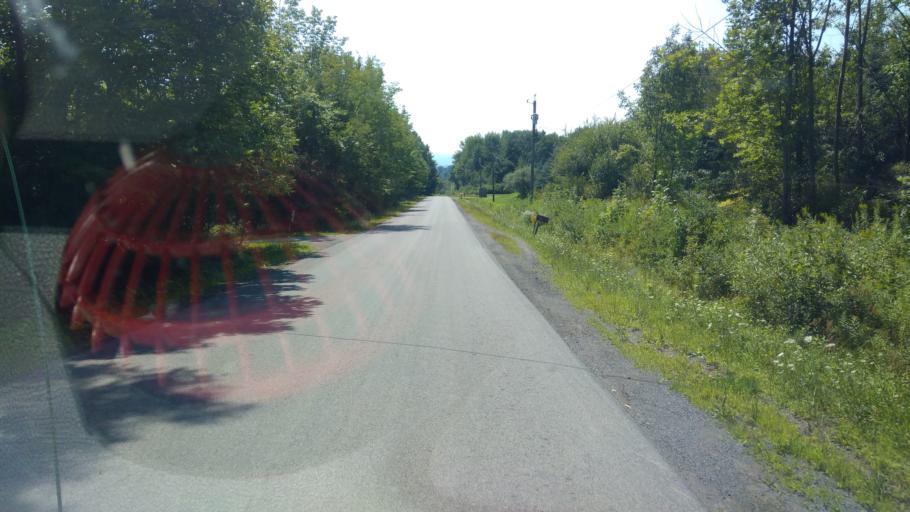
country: US
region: New York
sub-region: Allegany County
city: Belmont
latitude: 42.3459
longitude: -78.0418
